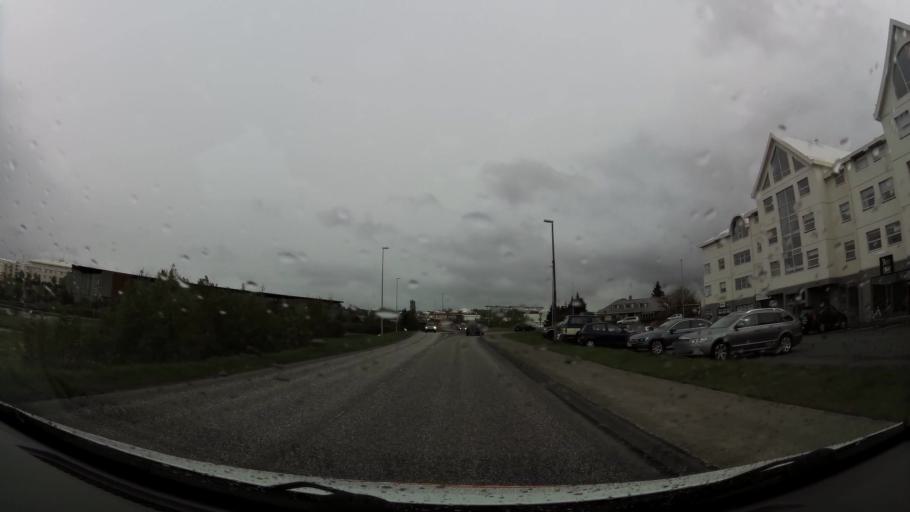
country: IS
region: Capital Region
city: Hafnarfjoerdur
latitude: 64.0671
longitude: -21.9445
